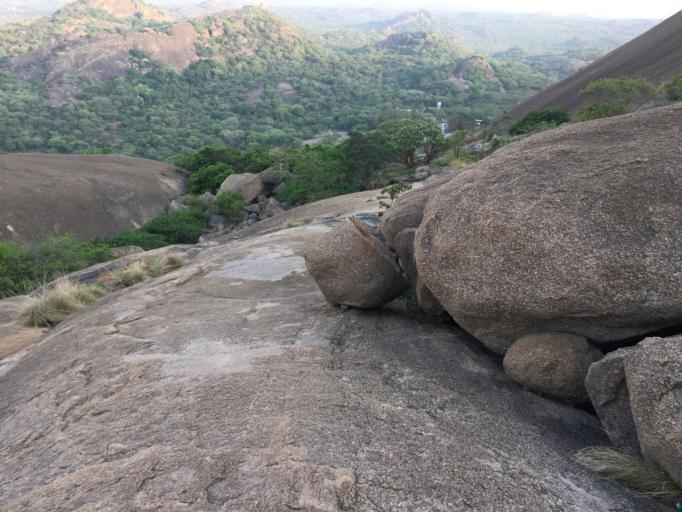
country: IN
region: Karnataka
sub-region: Ramanagara
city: Magadi
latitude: 12.9225
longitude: 77.2980
